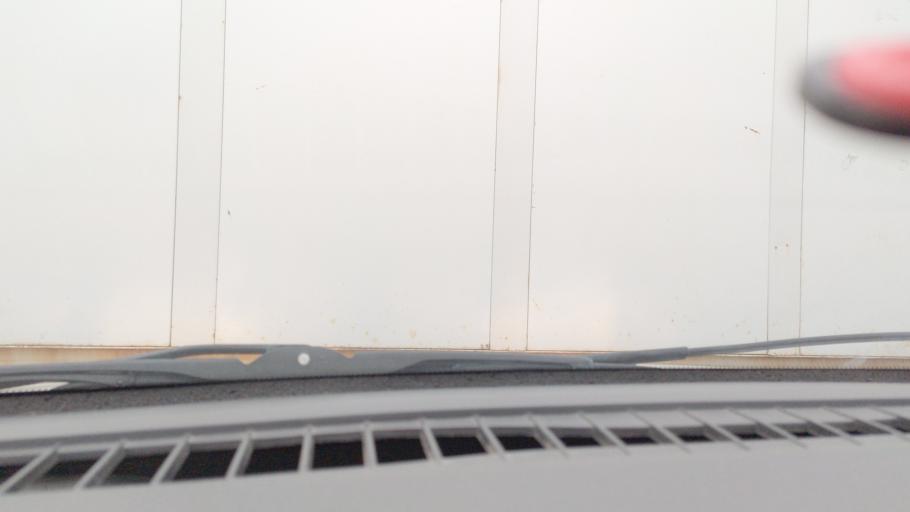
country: RU
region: Orenburg
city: Orenburg
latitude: 51.8115
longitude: 55.1776
